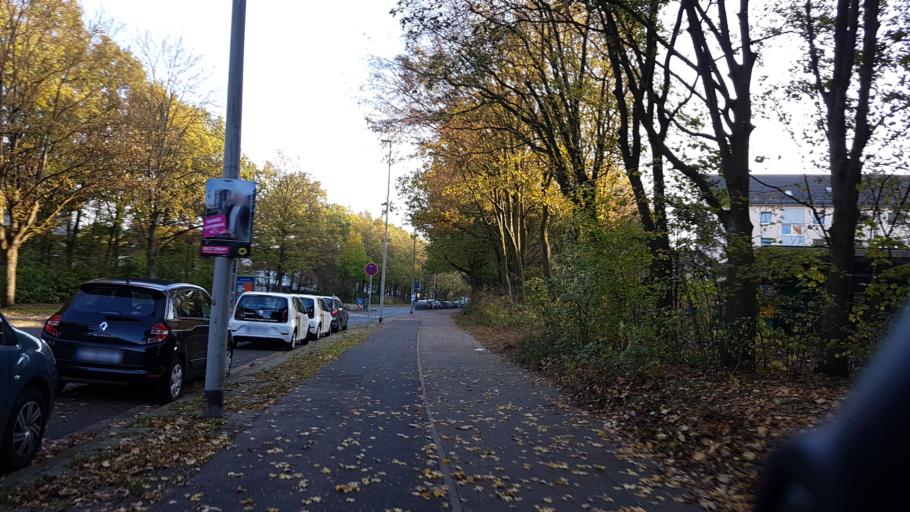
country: DE
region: Lower Saxony
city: Hemmingen
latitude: 52.3324
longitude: 9.7014
